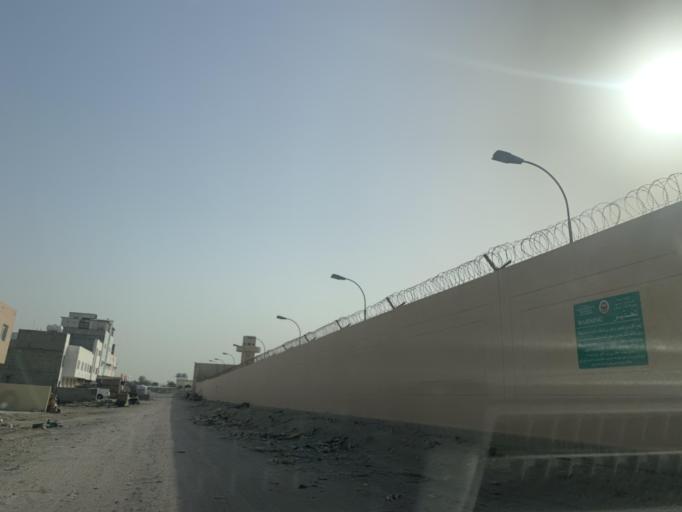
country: BH
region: Central Governorate
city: Madinat Hamad
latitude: 26.1458
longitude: 50.4825
